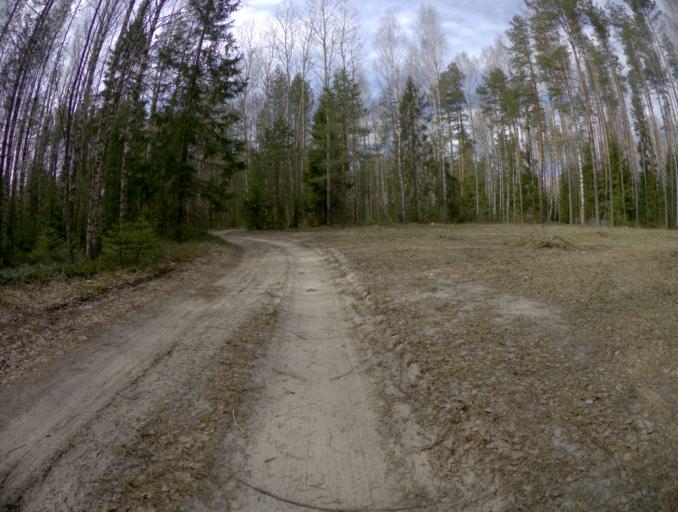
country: RU
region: Vladimir
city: Urshel'skiy
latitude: 55.8662
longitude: 40.1976
